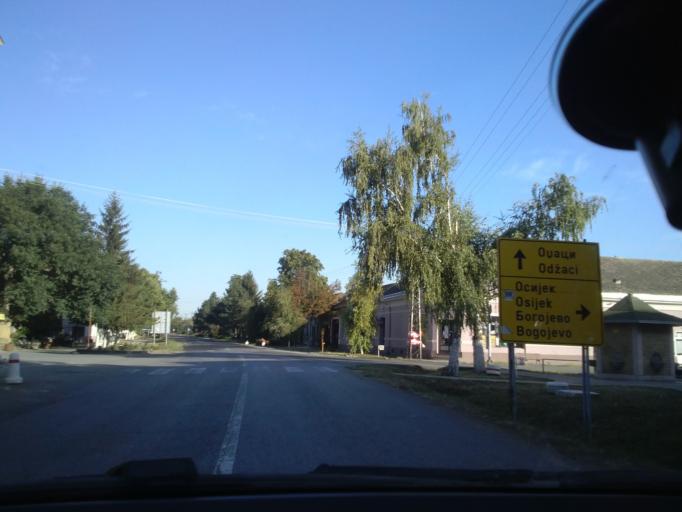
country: RS
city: Doroslovo
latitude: 45.5587
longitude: 19.2016
